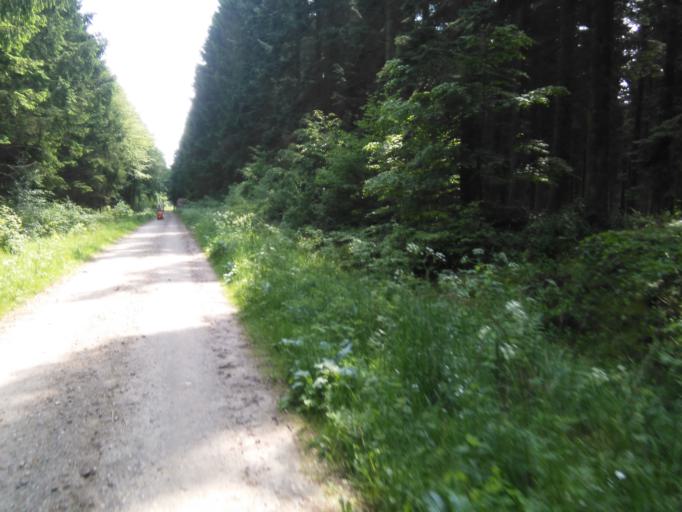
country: DK
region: Central Jutland
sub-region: Favrskov Kommune
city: Hinnerup
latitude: 56.2608
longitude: 10.0532
